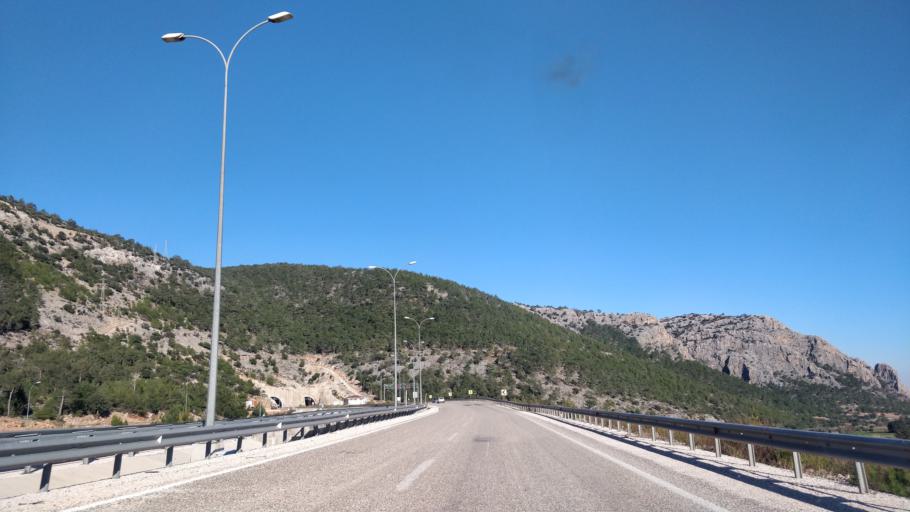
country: TR
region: Mersin
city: Akdere
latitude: 36.2556
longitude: 33.7875
